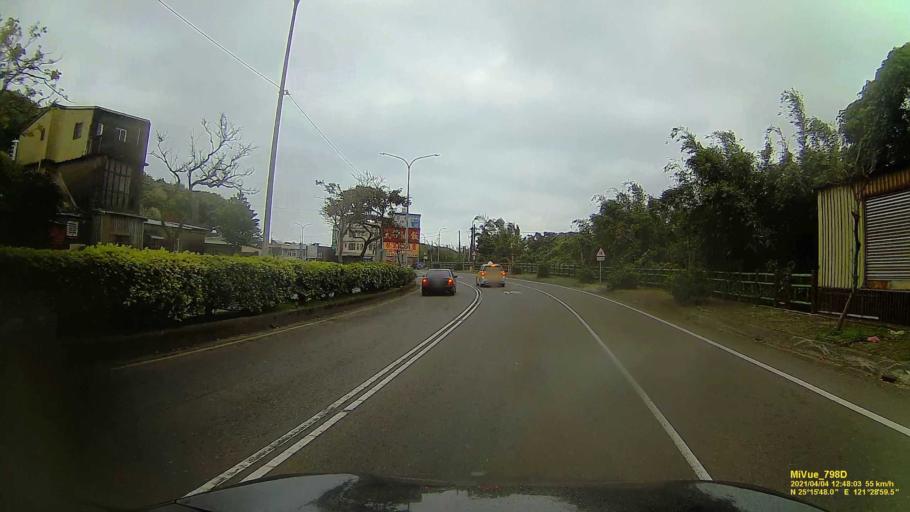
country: TW
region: Taipei
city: Taipei
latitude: 25.2635
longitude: 121.4829
